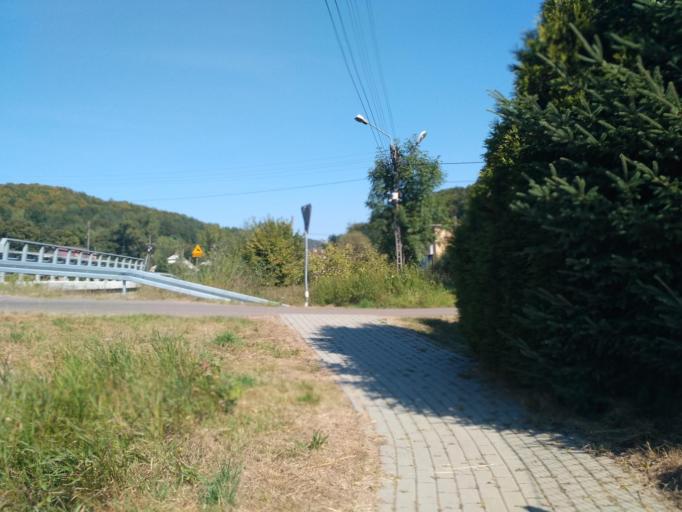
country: PL
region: Subcarpathian Voivodeship
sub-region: Powiat brzozowski
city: Grabownica Starzenska
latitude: 49.6651
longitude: 22.0829
